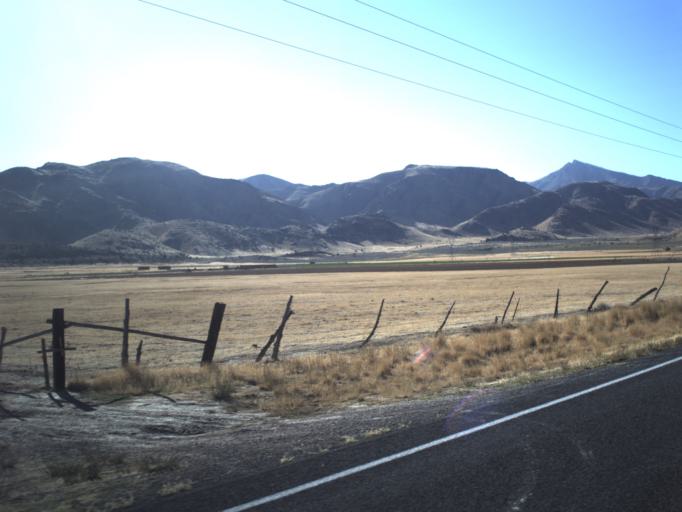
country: US
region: Utah
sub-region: Millard County
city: Delta
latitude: 39.5066
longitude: -112.2692
